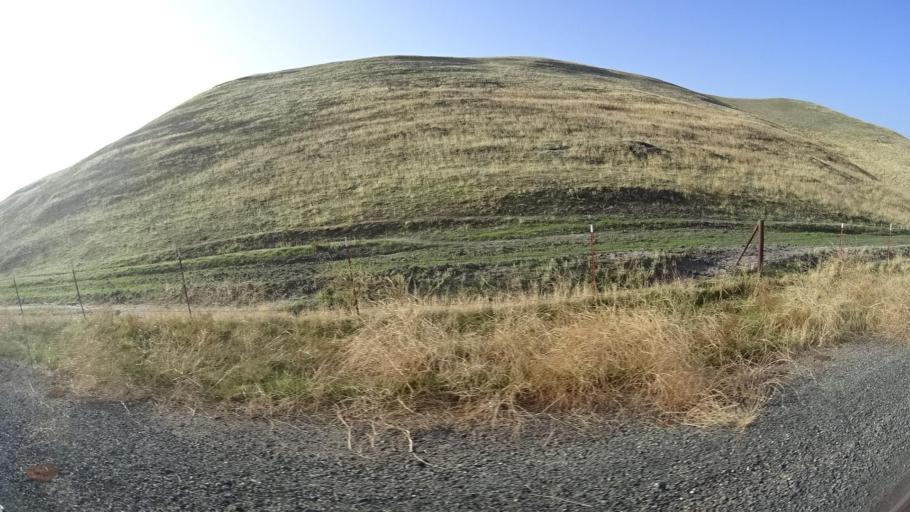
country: US
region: California
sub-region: Tulare County
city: Richgrove
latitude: 35.7462
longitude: -118.9288
